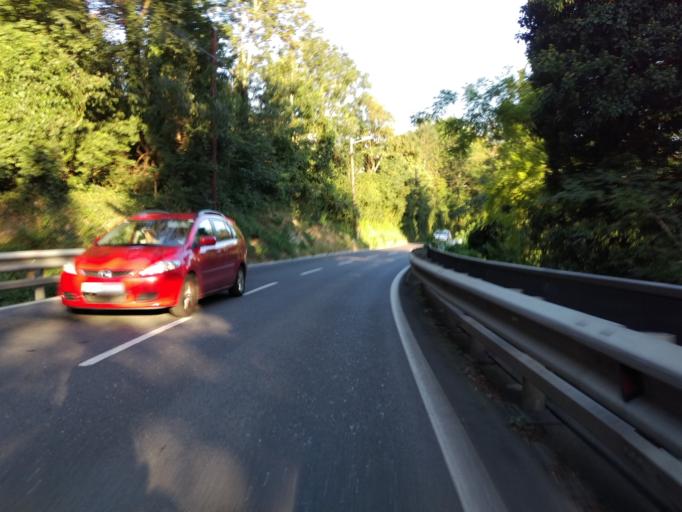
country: AT
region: Styria
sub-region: Graz Stadt
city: Wetzelsdorf
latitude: 47.0608
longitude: 15.3830
